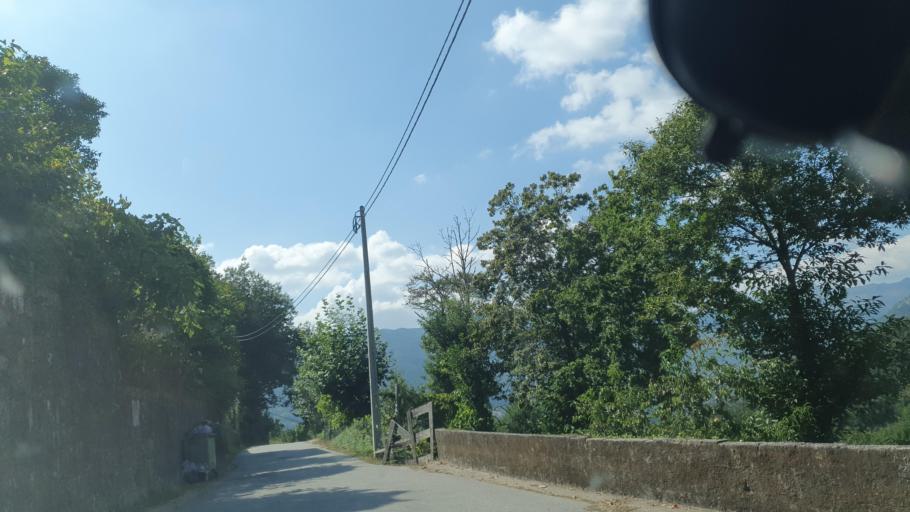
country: PT
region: Braga
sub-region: Vieira do Minho
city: Real
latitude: 41.6741
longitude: -8.1633
